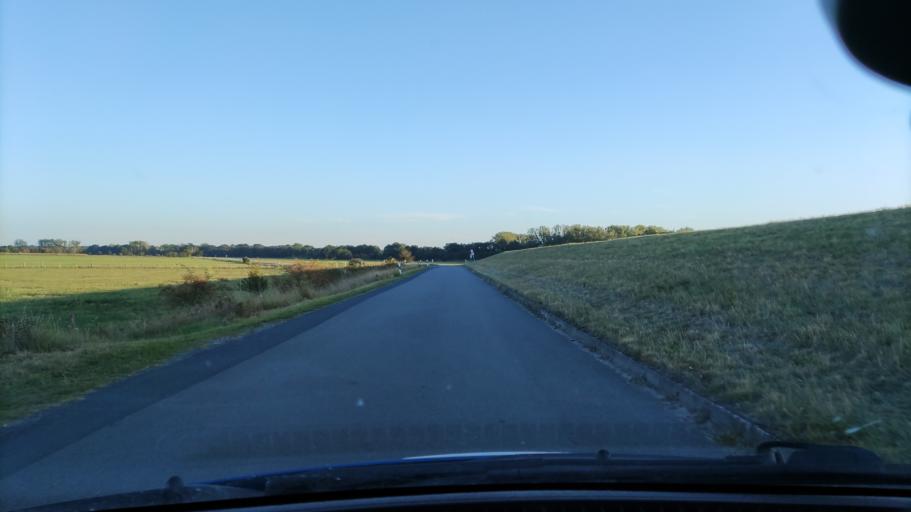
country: DE
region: Lower Saxony
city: Hitzacker
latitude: 53.1247
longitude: 11.0646
